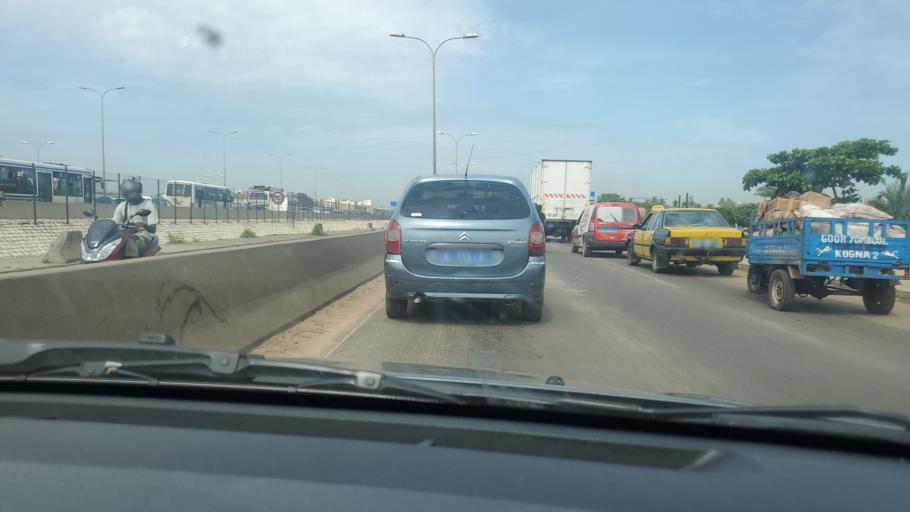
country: SN
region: Dakar
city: Pikine
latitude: 14.7466
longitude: -17.4185
